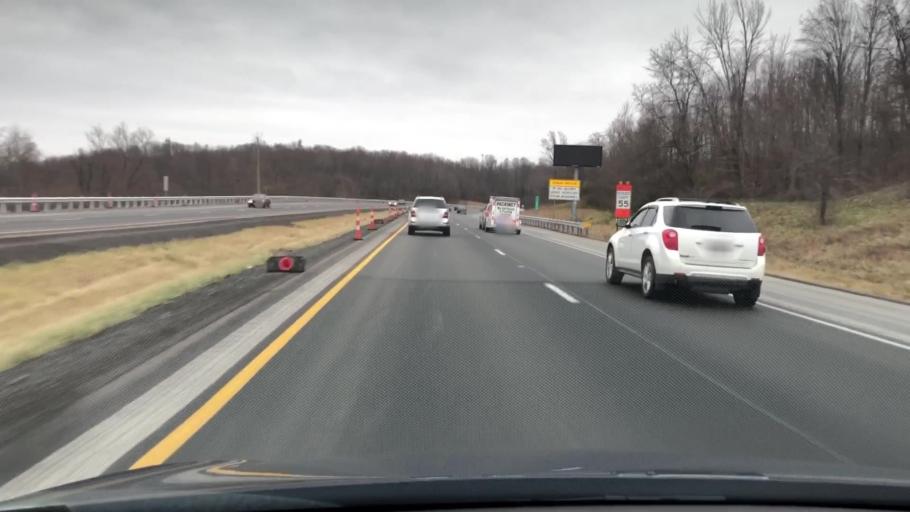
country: US
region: West Virginia
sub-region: Monongalia County
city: Star City
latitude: 39.6893
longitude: -80.0411
